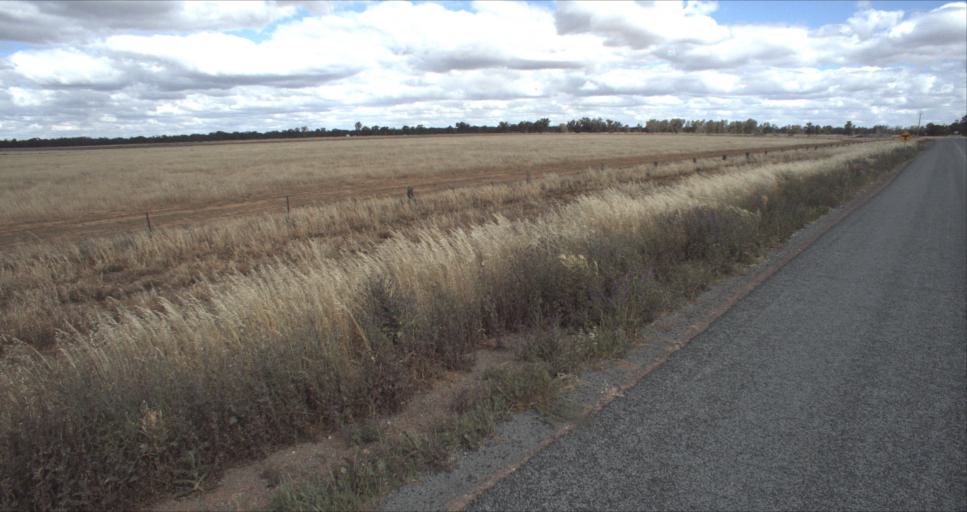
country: AU
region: New South Wales
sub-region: Leeton
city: Leeton
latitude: -34.6950
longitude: 146.3430
